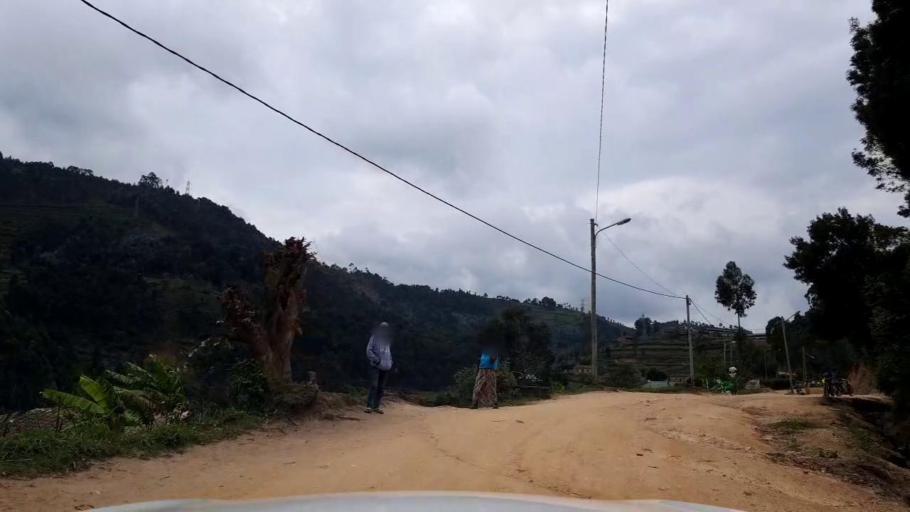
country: RW
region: Western Province
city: Kibuye
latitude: -1.9654
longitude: 29.3894
